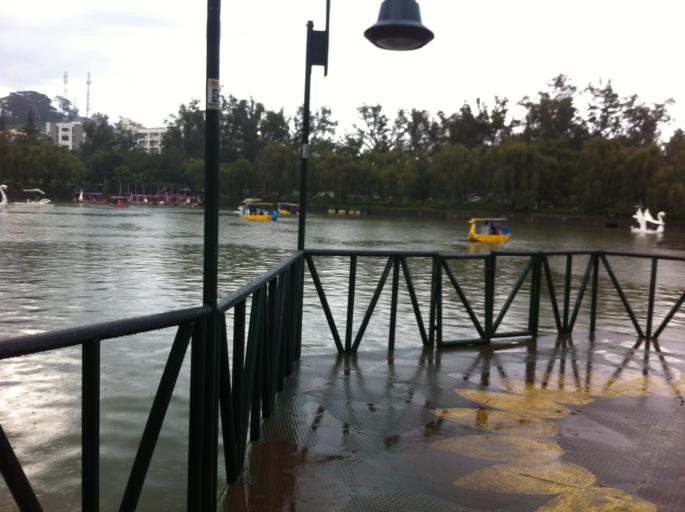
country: PH
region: Cordillera
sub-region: Baguio City
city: Baguio
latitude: 16.4105
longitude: 120.5944
